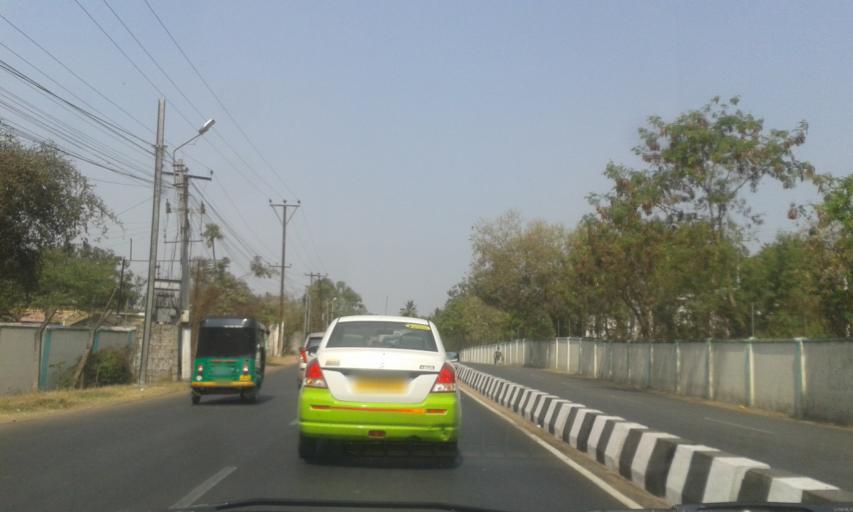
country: IN
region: Telangana
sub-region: Rangareddi
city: Secunderabad
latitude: 17.4893
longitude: 78.5124
